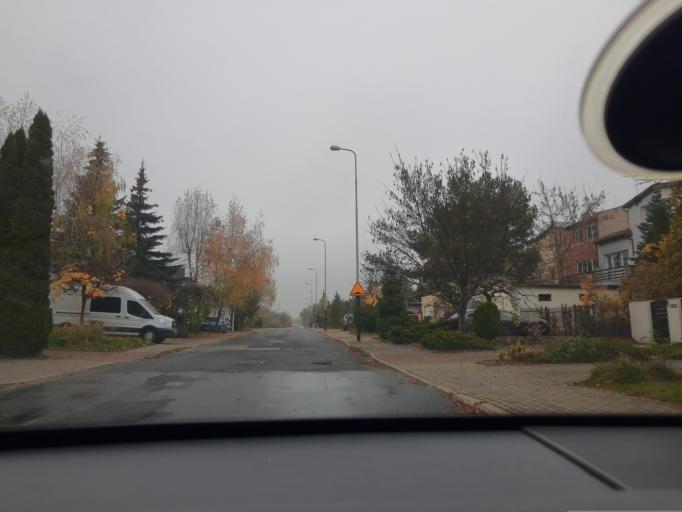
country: PL
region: Lodz Voivodeship
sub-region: Powiat pabianicki
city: Konstantynow Lodzki
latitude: 51.7430
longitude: 19.3783
